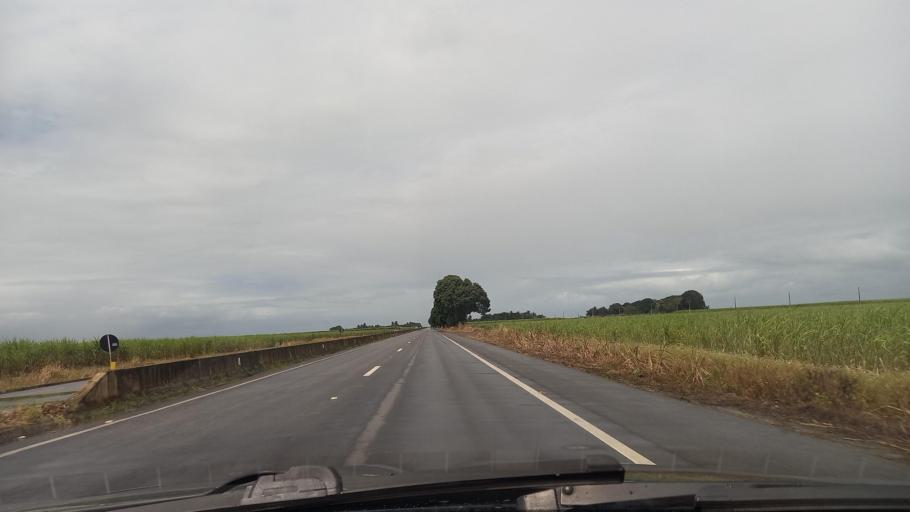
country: BR
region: Alagoas
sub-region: Campo Alegre
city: Campo Alegre
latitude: -9.8091
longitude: -36.2592
